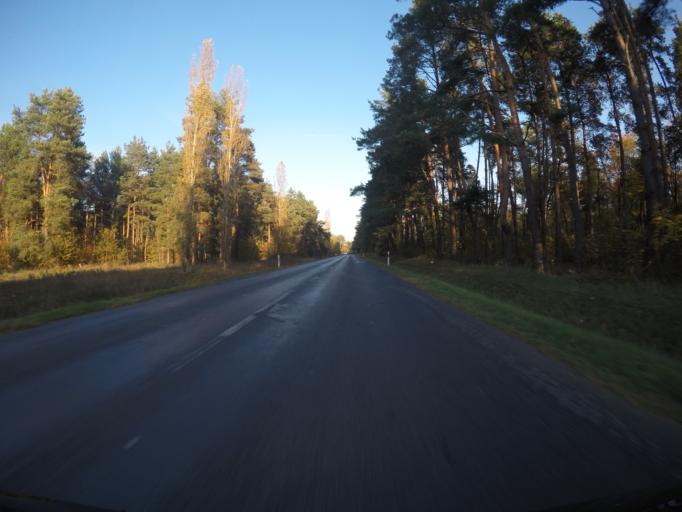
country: HU
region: Somogy
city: Barcs
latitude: 45.9791
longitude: 17.5747
